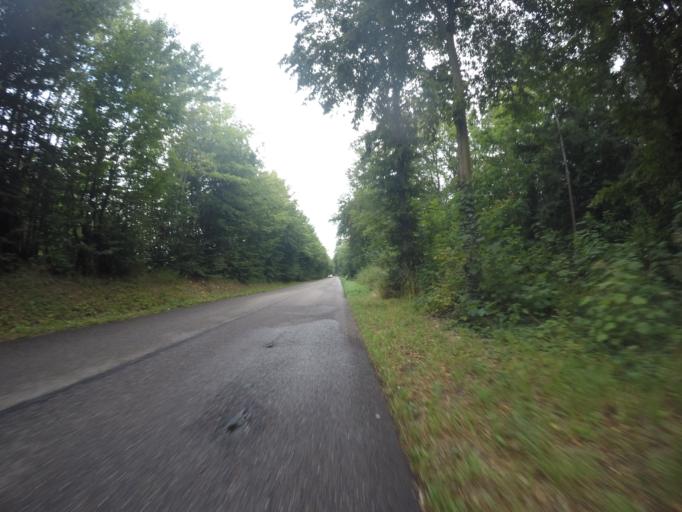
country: DE
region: Baden-Wuerttemberg
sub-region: Regierungsbezirk Stuttgart
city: Stuttgart-Ost
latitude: 48.7373
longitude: 9.1978
